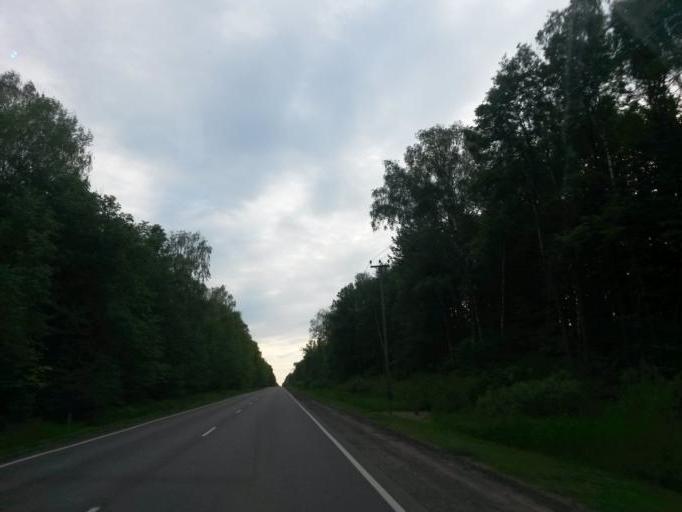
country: RU
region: Moskovskaya
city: Barybino
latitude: 55.2014
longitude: 37.8476
